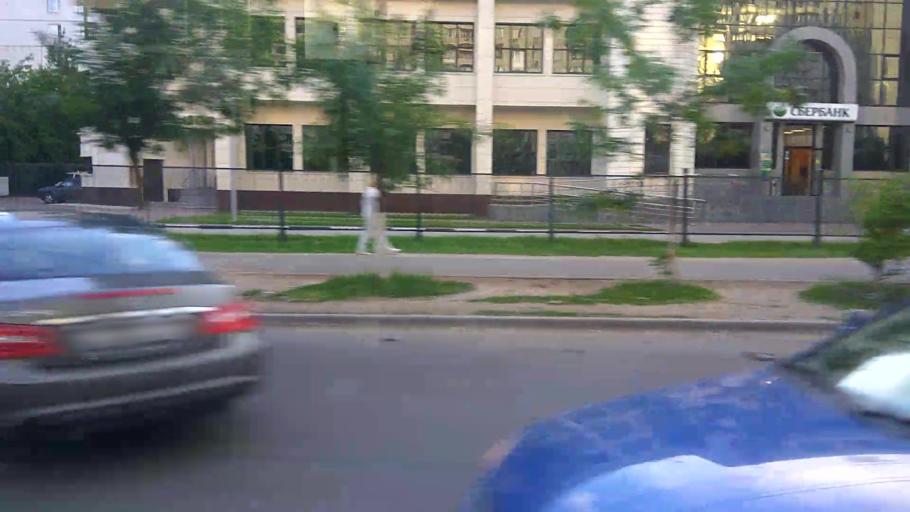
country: RU
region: Moskovskaya
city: Yubileyny
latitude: 55.9188
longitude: 37.8681
